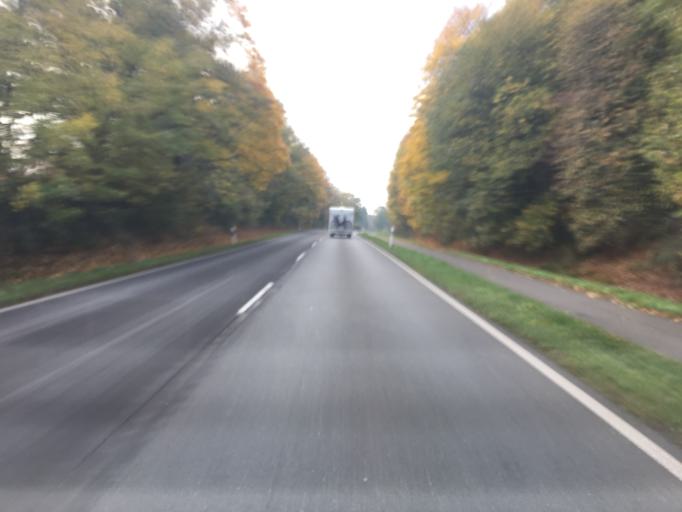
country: DE
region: North Rhine-Westphalia
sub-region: Regierungsbezirk Dusseldorf
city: Sonsbeck
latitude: 51.6298
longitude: 6.3998
